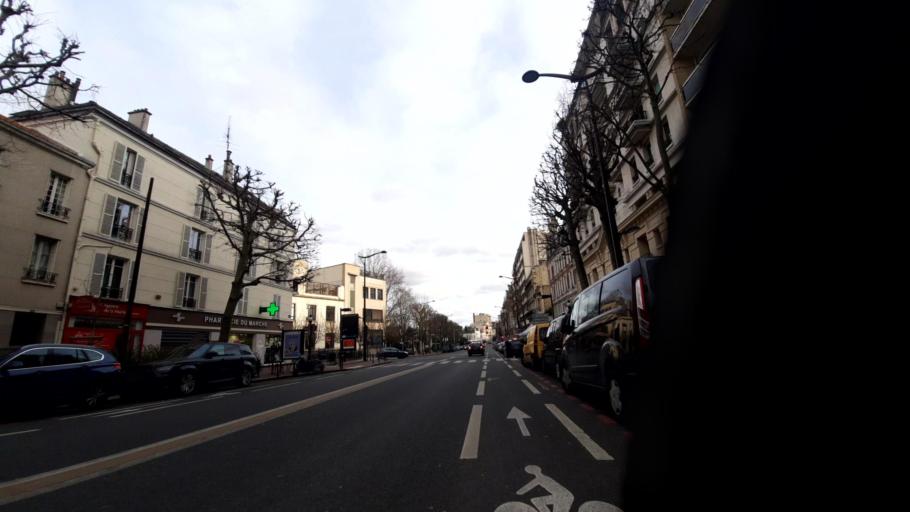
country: FR
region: Ile-de-France
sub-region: Departement du Val-de-Marne
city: Charenton-le-Pont
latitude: 48.8226
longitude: 2.4120
